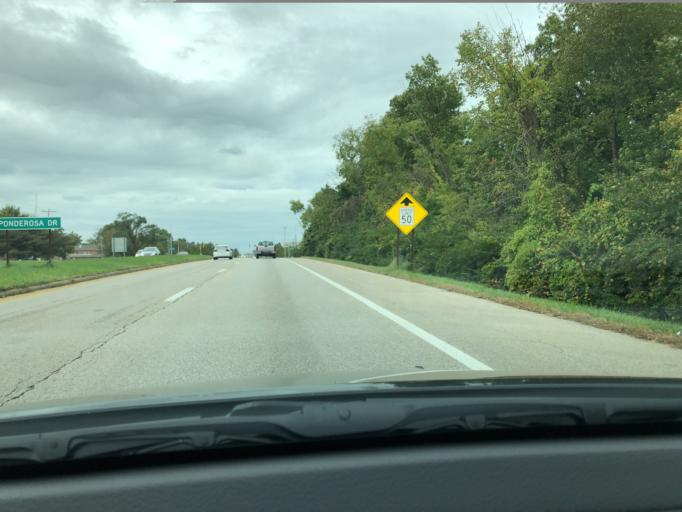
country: US
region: Ohio
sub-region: Franklin County
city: Minerva Park
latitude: 40.0816
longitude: -82.9347
